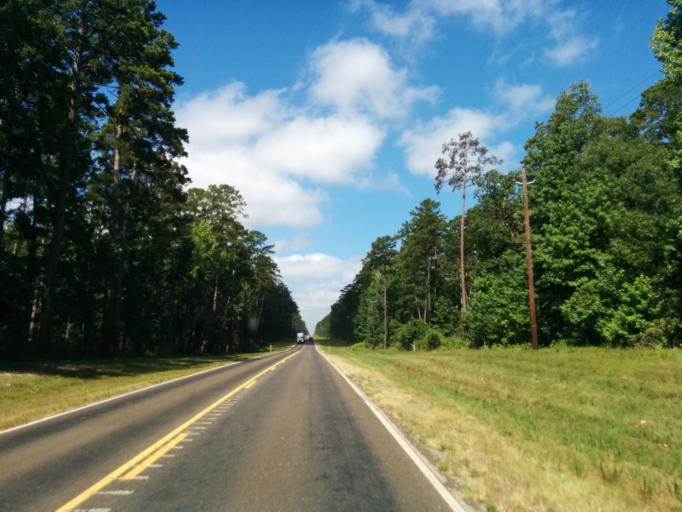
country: US
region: Texas
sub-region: Houston County
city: Hickory Creek
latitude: 31.3528
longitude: -95.2242
